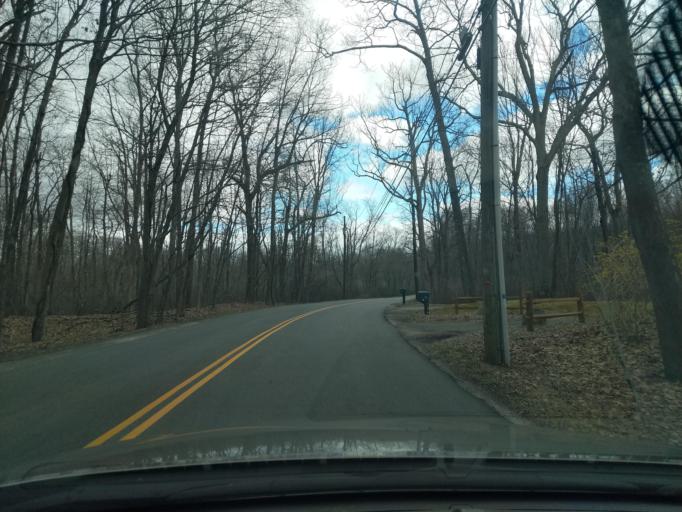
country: US
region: Connecticut
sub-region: Fairfield County
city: Newtown
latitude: 41.3547
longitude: -73.3227
